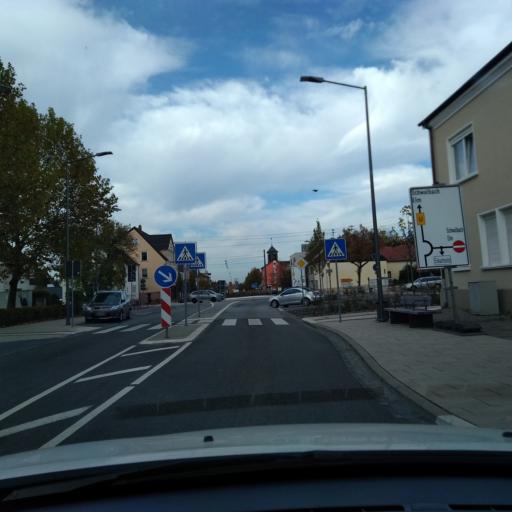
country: DE
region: Saarland
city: Ensdorf
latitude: 49.3043
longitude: 6.7783
